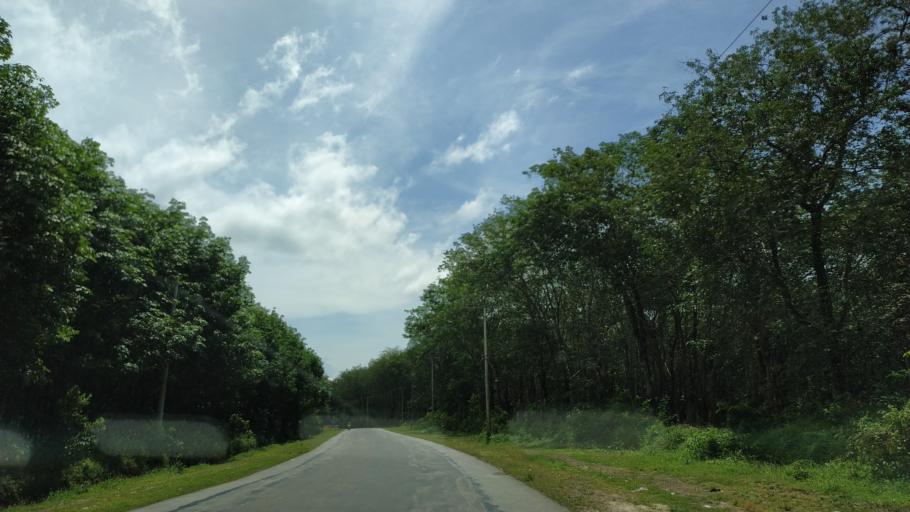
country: MM
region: Tanintharyi
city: Dawei
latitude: 14.1218
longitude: 98.1356
